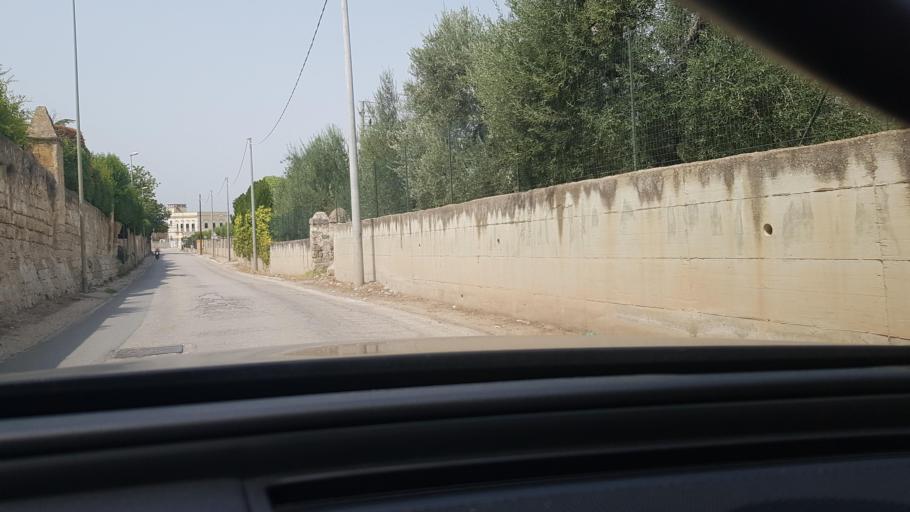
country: IT
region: Apulia
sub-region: Provincia di Barletta - Andria - Trani
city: Andria
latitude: 41.2326
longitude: 16.2704
